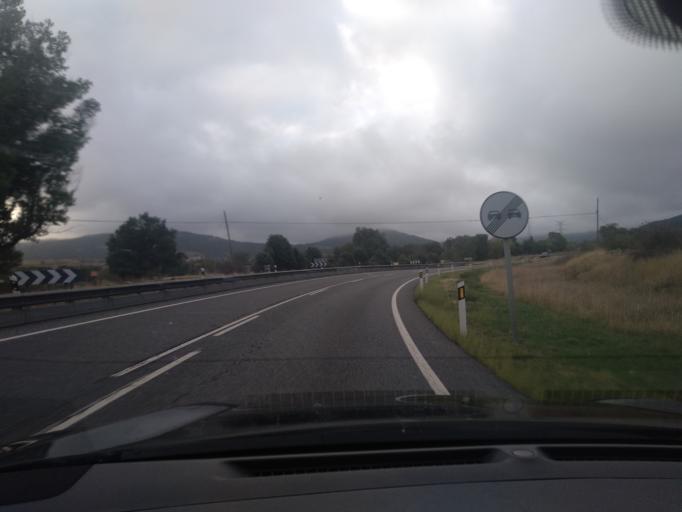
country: ES
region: Castille and Leon
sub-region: Provincia de Segovia
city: Otero de Herreros
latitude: 40.7508
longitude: -4.1997
